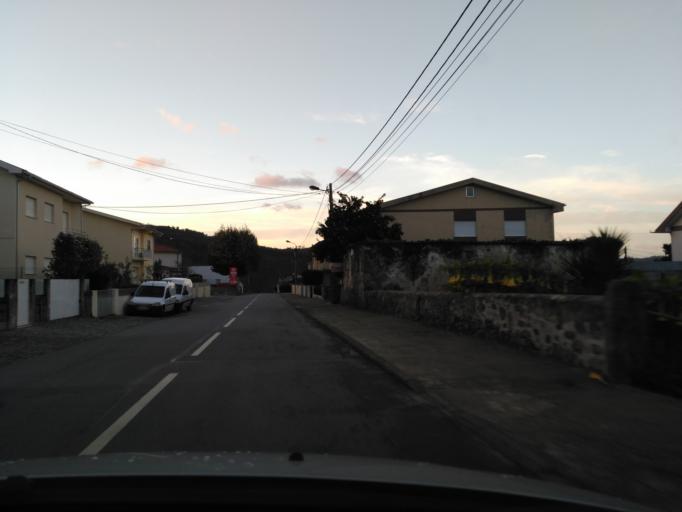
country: PT
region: Braga
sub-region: Braga
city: Braga
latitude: 41.5296
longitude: -8.4102
